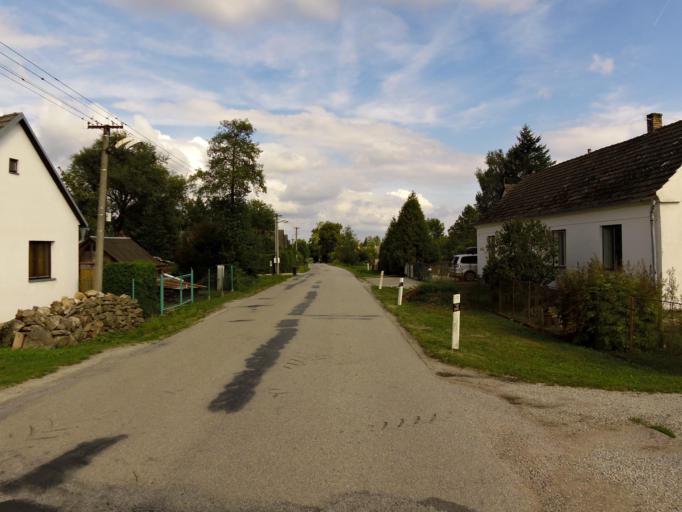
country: CZ
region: Jihocesky
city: Suchdol nad Luznici
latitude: 48.8897
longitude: 14.8514
